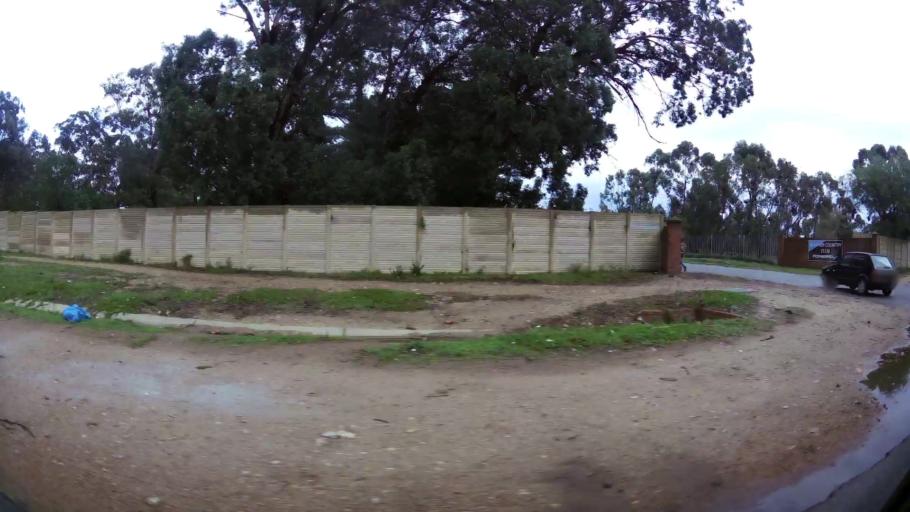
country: ZA
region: Eastern Cape
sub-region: Nelson Mandela Bay Metropolitan Municipality
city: Port Elizabeth
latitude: -33.9916
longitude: 25.5796
